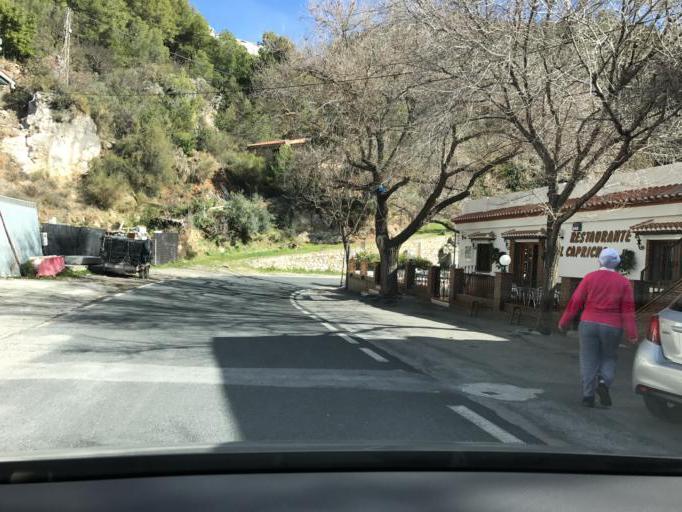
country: ES
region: Andalusia
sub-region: Provincia de Granada
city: Otivar
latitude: 36.8184
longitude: -3.6803
